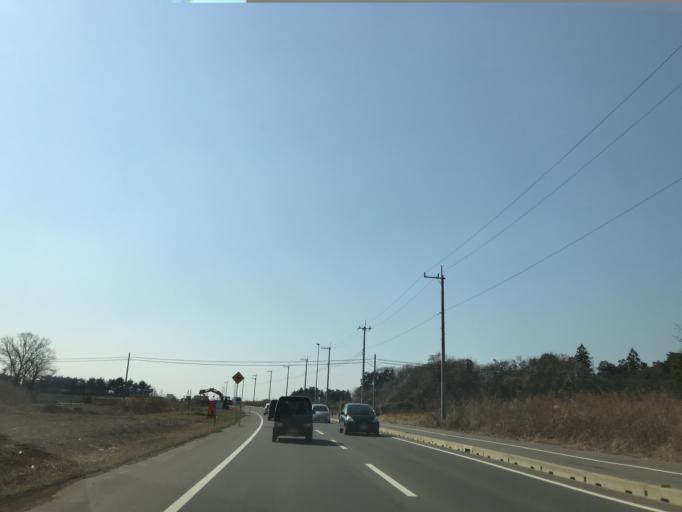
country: JP
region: Ibaraki
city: Mitsukaido
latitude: 36.0110
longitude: 140.0342
